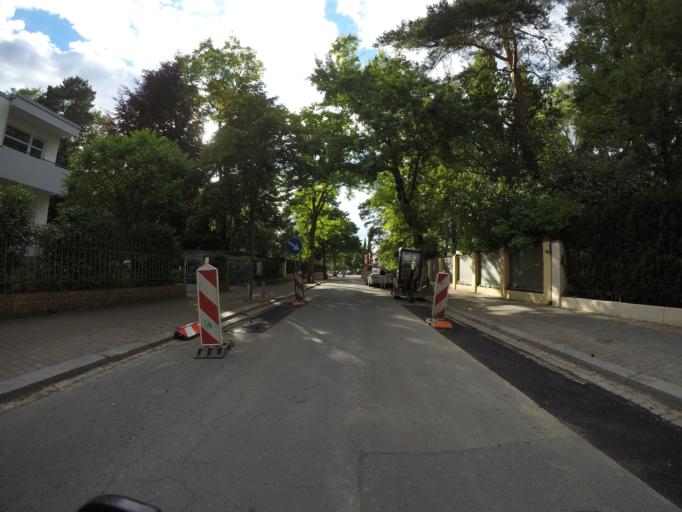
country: DE
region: Berlin
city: Grunewald
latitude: 52.4863
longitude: 13.2772
